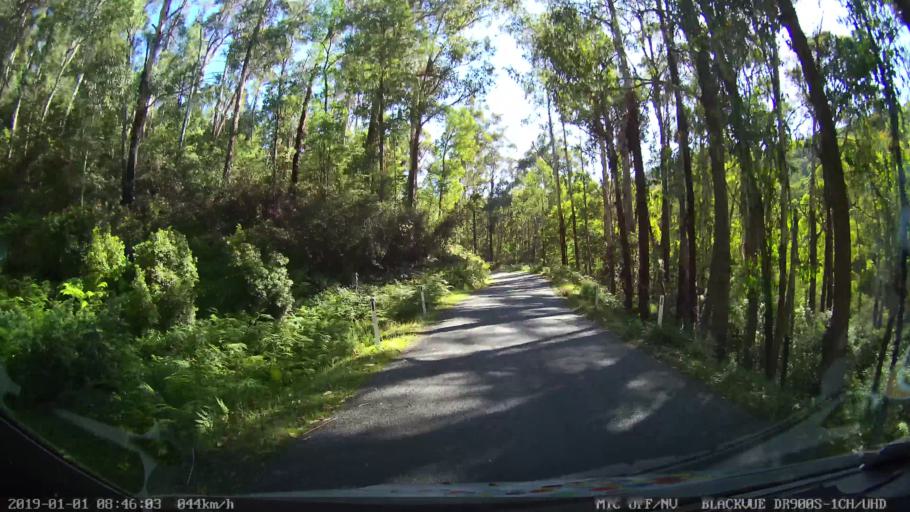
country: AU
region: New South Wales
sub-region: Snowy River
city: Jindabyne
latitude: -36.3020
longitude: 148.1914
